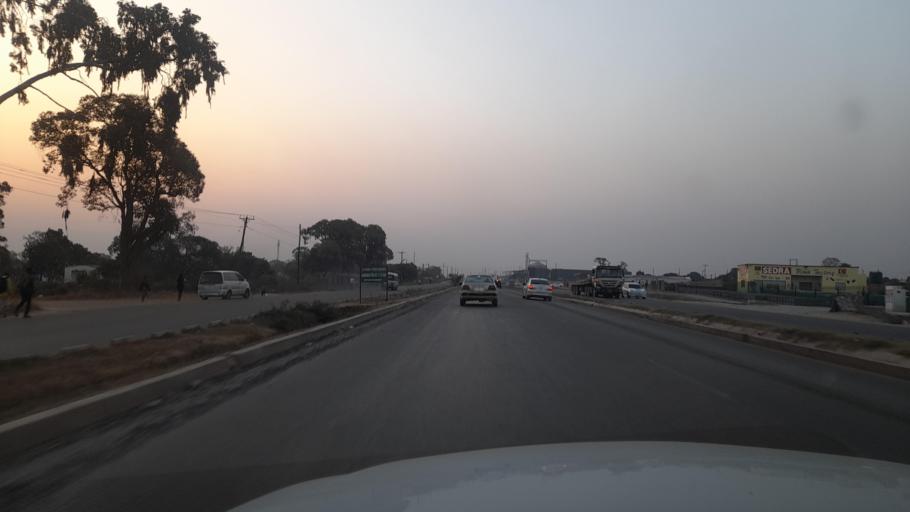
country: ZM
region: Copperbelt
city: Kitwe
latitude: -12.7818
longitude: 28.1963
